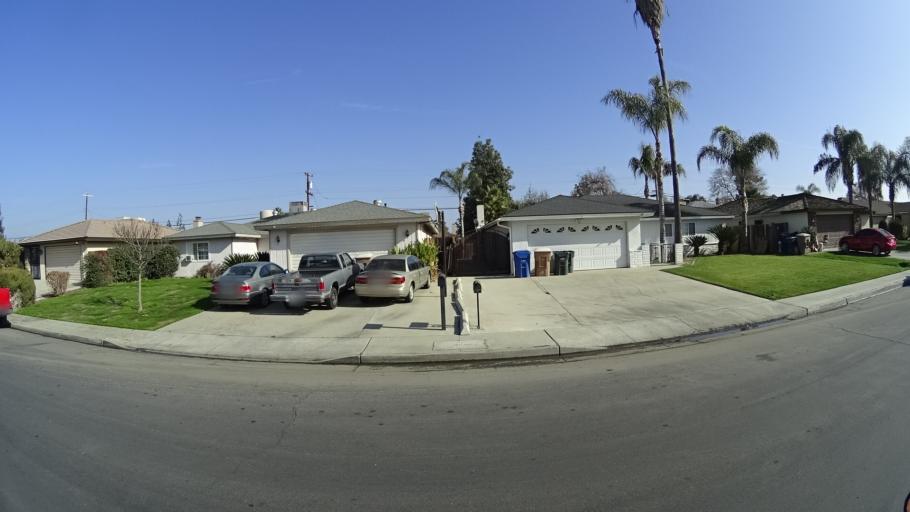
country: US
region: California
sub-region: Kern County
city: Bakersfield
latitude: 35.3355
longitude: -119.0572
